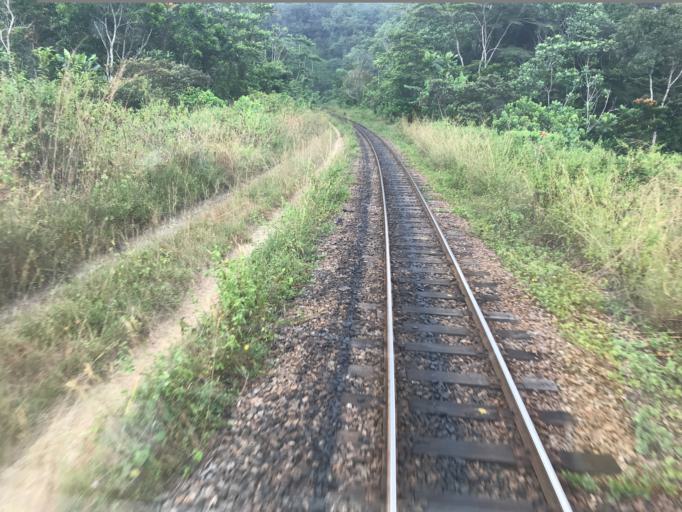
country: CM
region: Centre
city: Eseka
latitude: 3.5961
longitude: 10.8302
